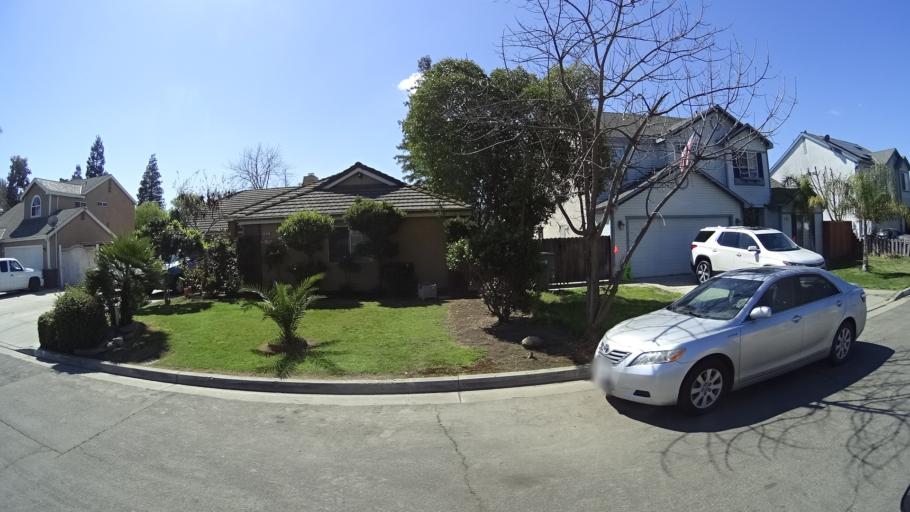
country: US
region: California
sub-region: Fresno County
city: West Park
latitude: 36.7911
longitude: -119.8768
